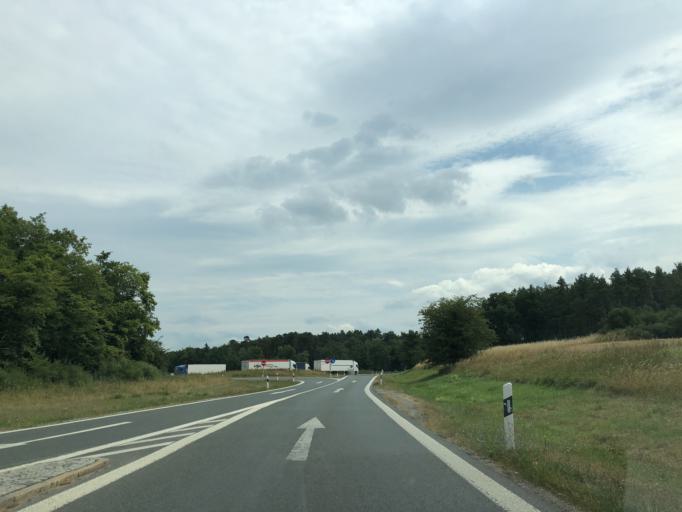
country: DE
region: Bavaria
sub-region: Regierungsbezirk Mittelfranken
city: Muhlhausen
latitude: 49.7371
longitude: 10.7907
